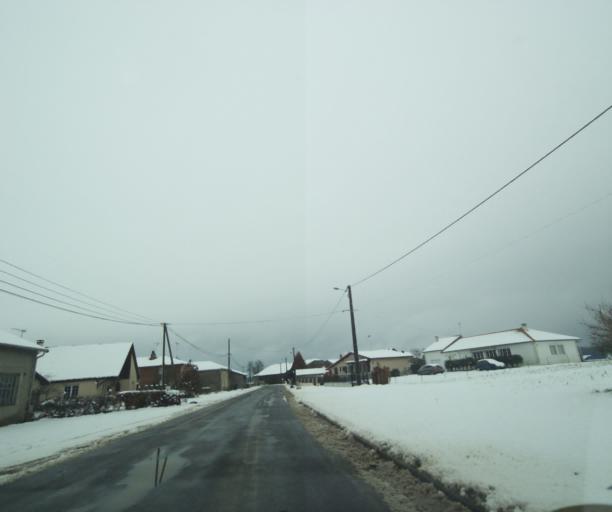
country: FR
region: Champagne-Ardenne
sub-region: Departement de la Haute-Marne
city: Montier-en-Der
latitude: 48.4405
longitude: 4.8027
